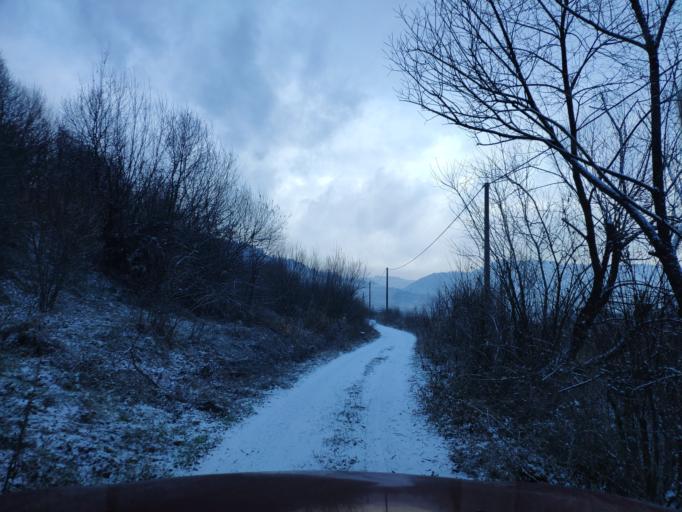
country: SK
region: Kosicky
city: Spisska Nova Ves
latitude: 48.8280
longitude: 20.5985
